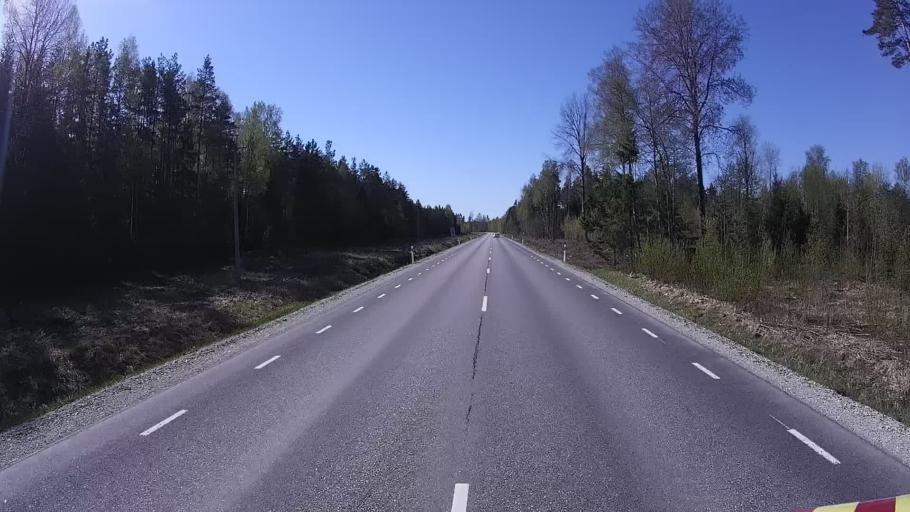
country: EE
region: Raplamaa
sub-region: Jaervakandi vald
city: Jarvakandi
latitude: 58.7626
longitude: 24.8143
